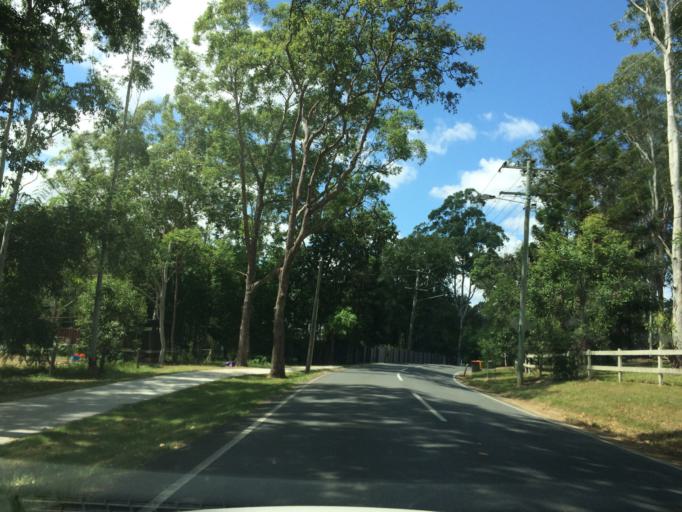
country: AU
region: Queensland
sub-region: Brisbane
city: Kenmore Hills
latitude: -27.4980
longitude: 152.9133
